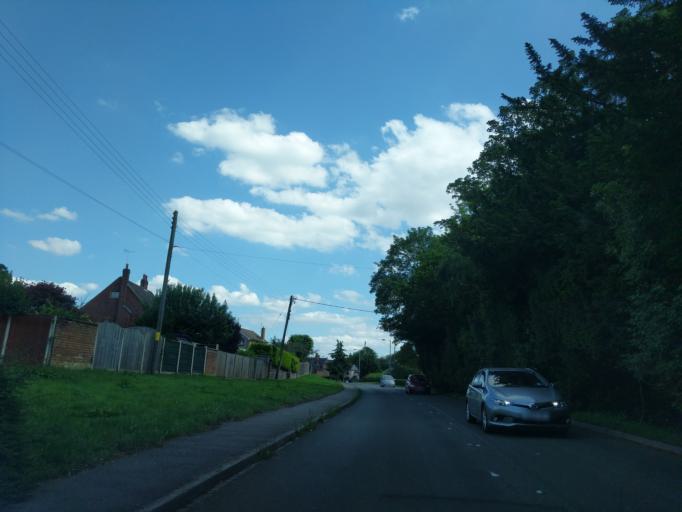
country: GB
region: England
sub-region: Staffordshire
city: Cheadle
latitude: 52.9442
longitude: -1.9759
